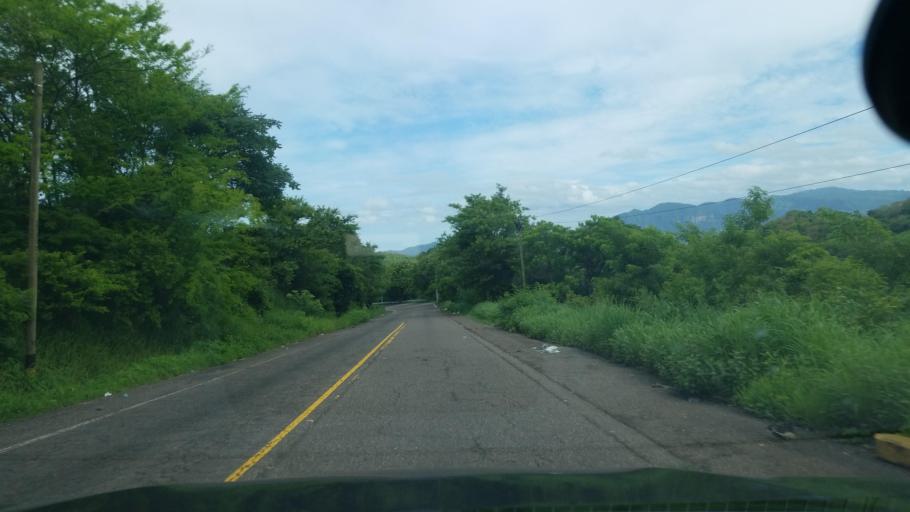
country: HN
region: Choluteca
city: Santa Ana de Yusguare
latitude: 13.3742
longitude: -87.0634
